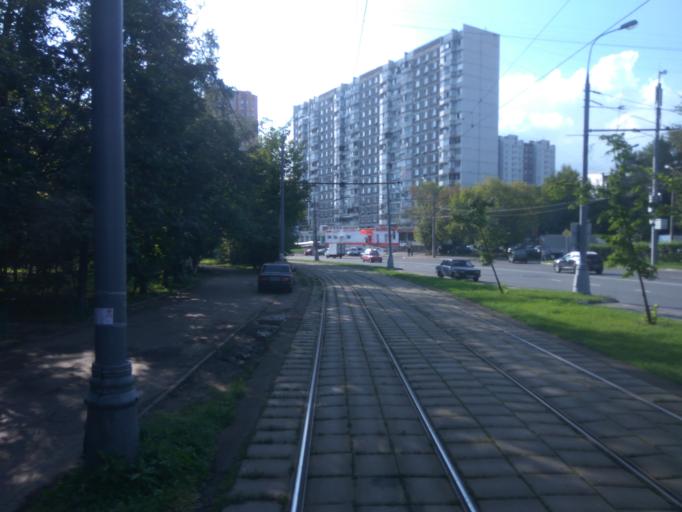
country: RU
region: Moskovskaya
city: Novogireyevo
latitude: 55.7537
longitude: 37.8018
